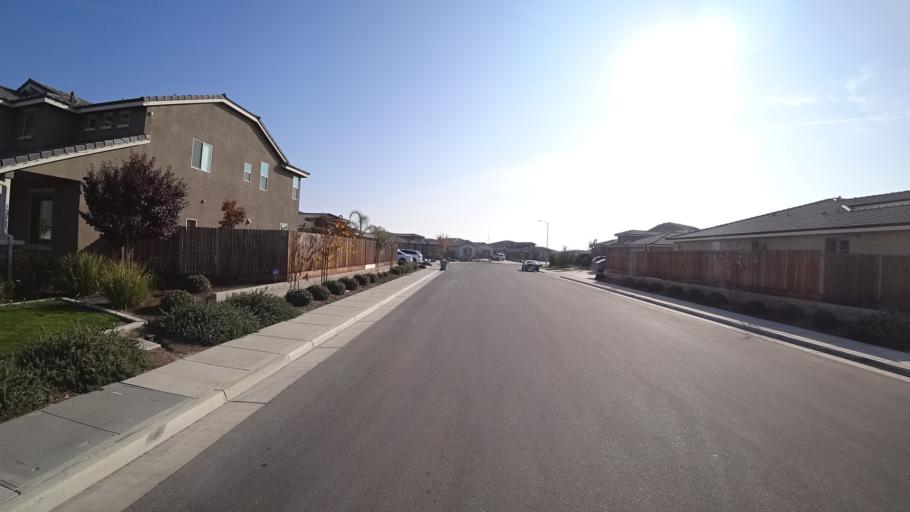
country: US
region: California
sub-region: Kern County
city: Rosedale
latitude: 35.3530
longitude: -119.1704
